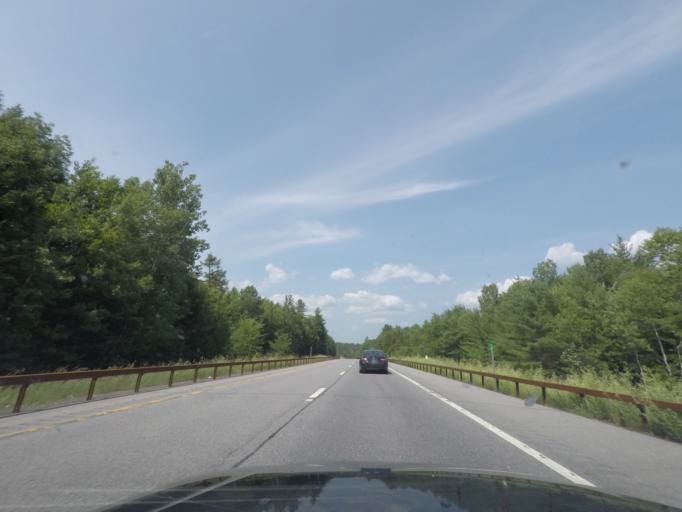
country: US
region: New York
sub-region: Warren County
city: Warrensburg
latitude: 43.8052
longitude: -73.7869
